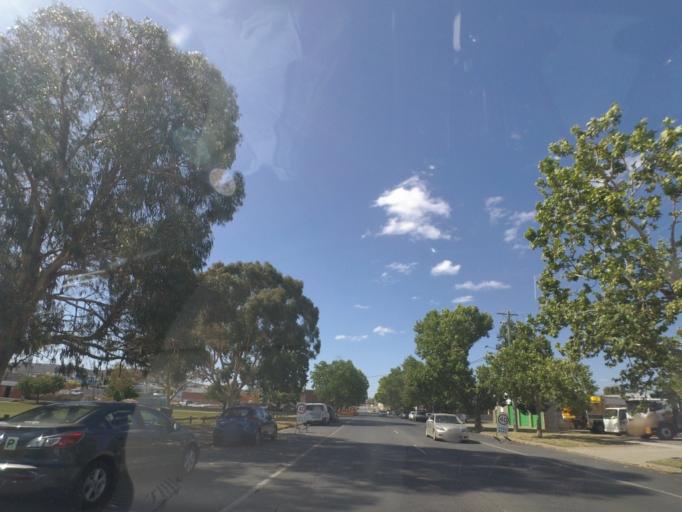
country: AU
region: New South Wales
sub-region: Albury Municipality
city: South Albury
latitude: -36.0865
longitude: 146.9146
